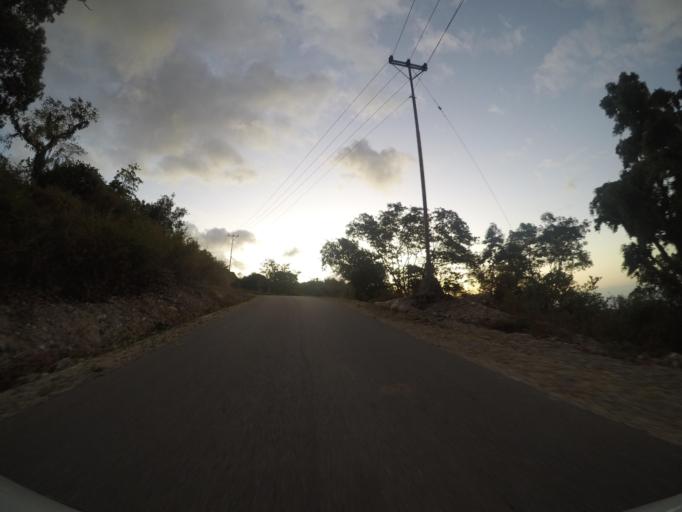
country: TL
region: Lautem
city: Lospalos
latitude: -8.3642
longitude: 127.0491
